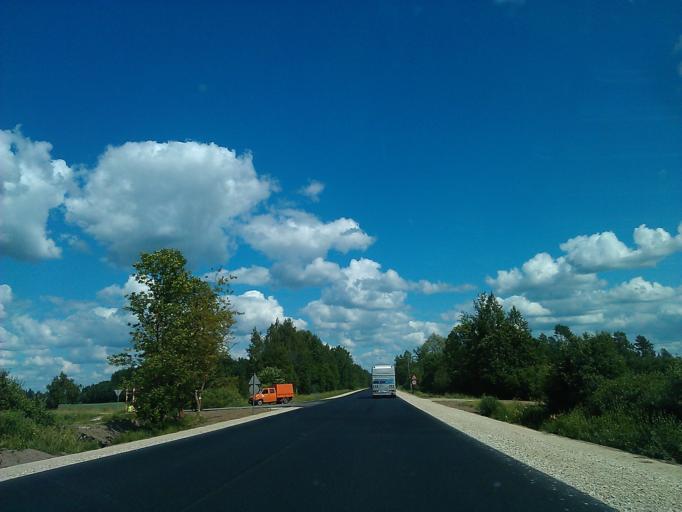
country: LV
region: Vilanu
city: Vilani
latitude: 56.5638
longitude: 27.0015
